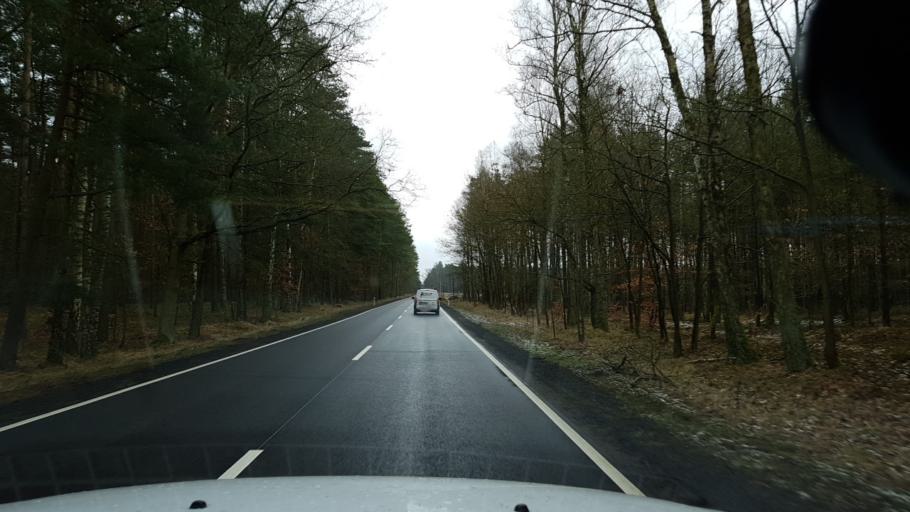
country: PL
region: West Pomeranian Voivodeship
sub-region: Powiat goleniowski
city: Stepnica
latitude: 53.6326
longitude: 14.6667
